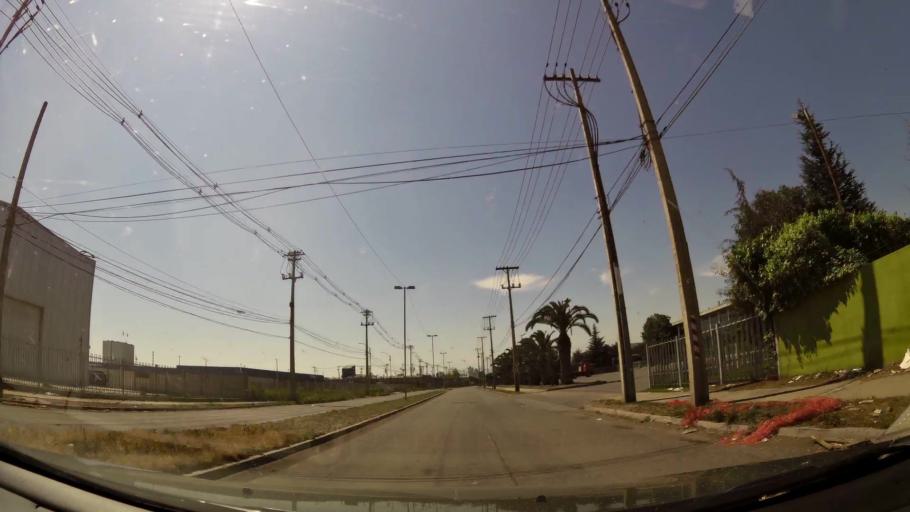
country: CL
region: Santiago Metropolitan
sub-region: Provincia de Santiago
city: Lo Prado
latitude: -33.3885
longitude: -70.7549
